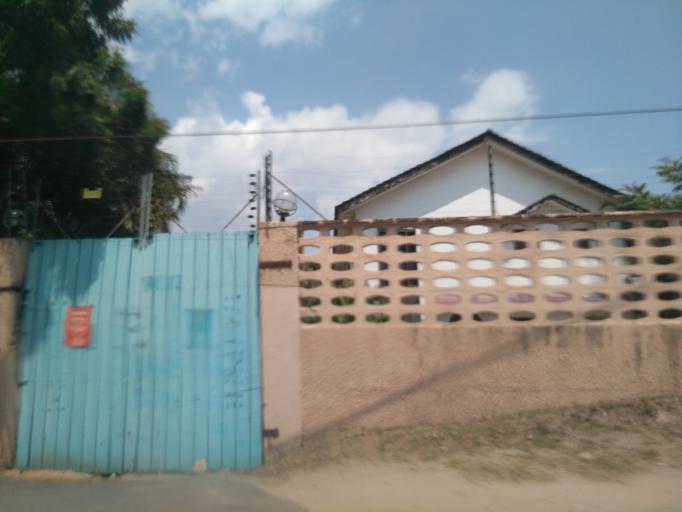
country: TZ
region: Dar es Salaam
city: Dar es Salaam
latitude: -6.8029
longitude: 39.2836
